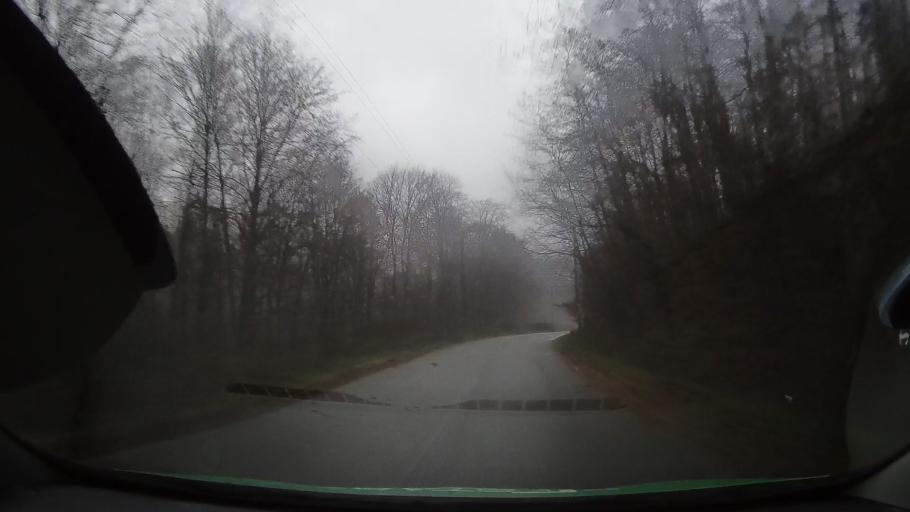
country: RO
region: Hunedoara
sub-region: Comuna Ribita
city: Ribita
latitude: 46.2474
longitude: 22.7492
